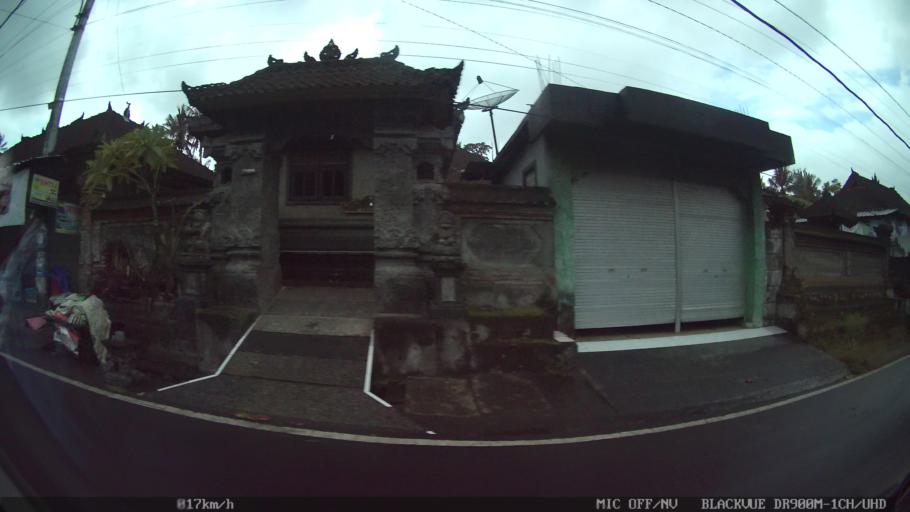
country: ID
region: Bali
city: Banjar Tebongkang
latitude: -8.5249
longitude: 115.2282
